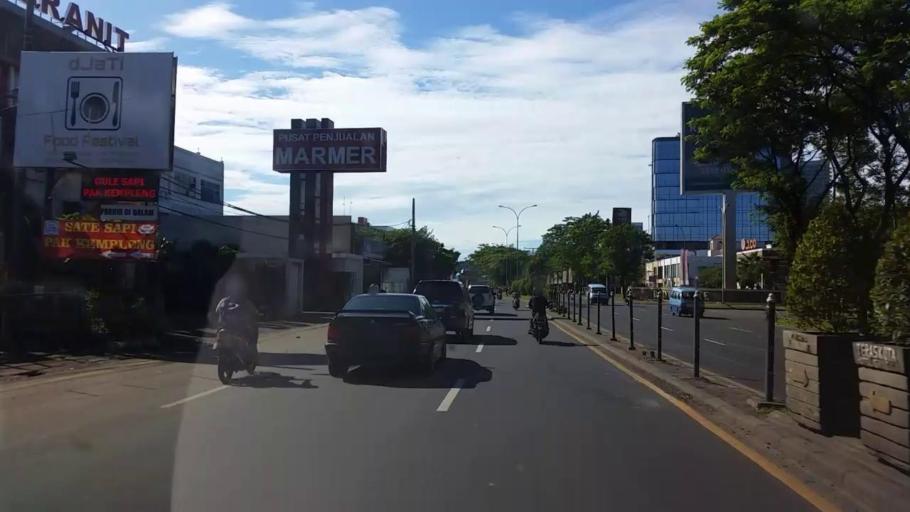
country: ID
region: West Java
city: Serpong
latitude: -6.2922
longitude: 106.6660
